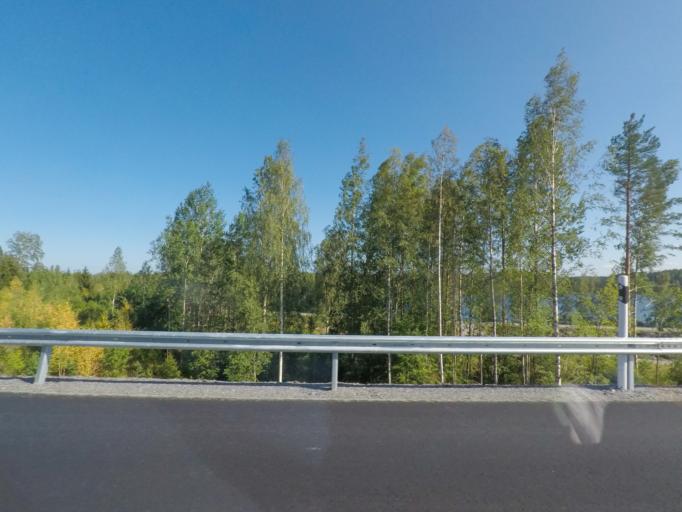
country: FI
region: Southern Savonia
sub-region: Mikkeli
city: Mikkeli
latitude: 61.7568
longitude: 27.5524
